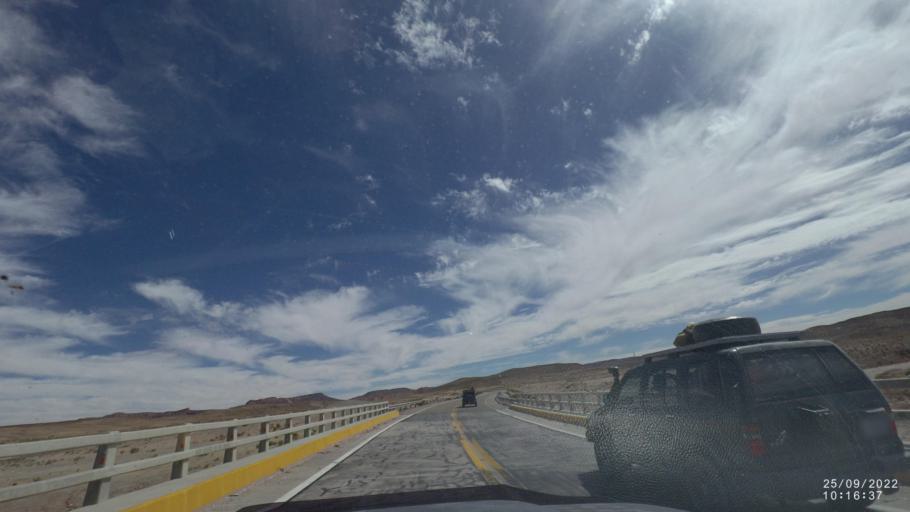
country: BO
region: Potosi
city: Colchani
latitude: -20.0275
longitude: -66.8697
